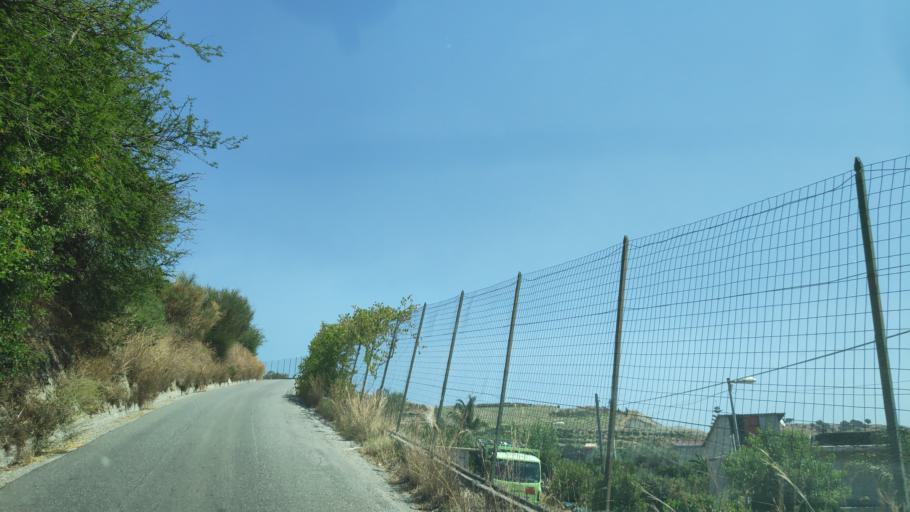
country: IT
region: Calabria
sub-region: Provincia di Reggio Calabria
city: Bova Marina
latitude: 37.9374
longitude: 15.9117
